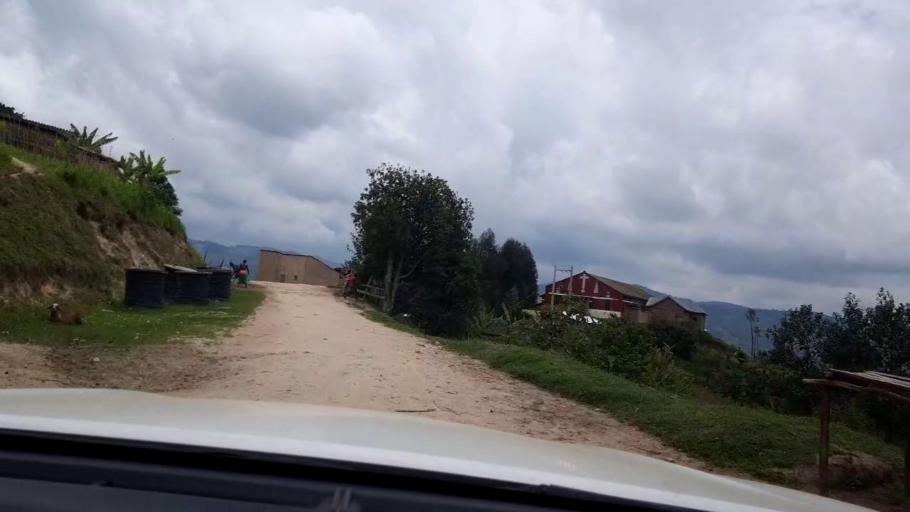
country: RW
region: Western Province
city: Kibuye
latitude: -1.8336
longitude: 29.5459
